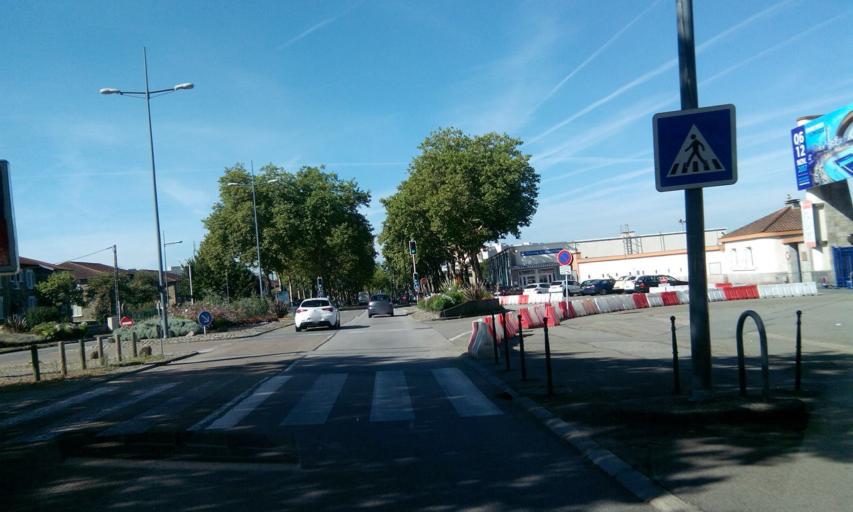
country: FR
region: Limousin
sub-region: Departement de la Haute-Vienne
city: Limoges
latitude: 45.8470
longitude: 1.2438
